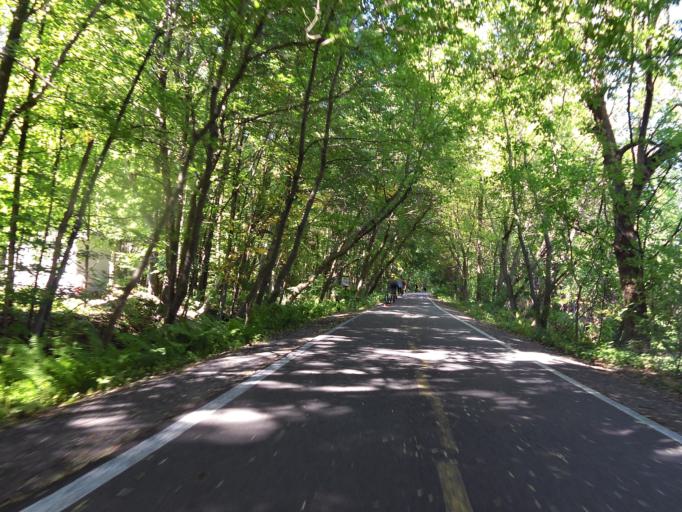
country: CA
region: Ontario
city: Bourget
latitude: 45.2627
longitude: -75.3658
